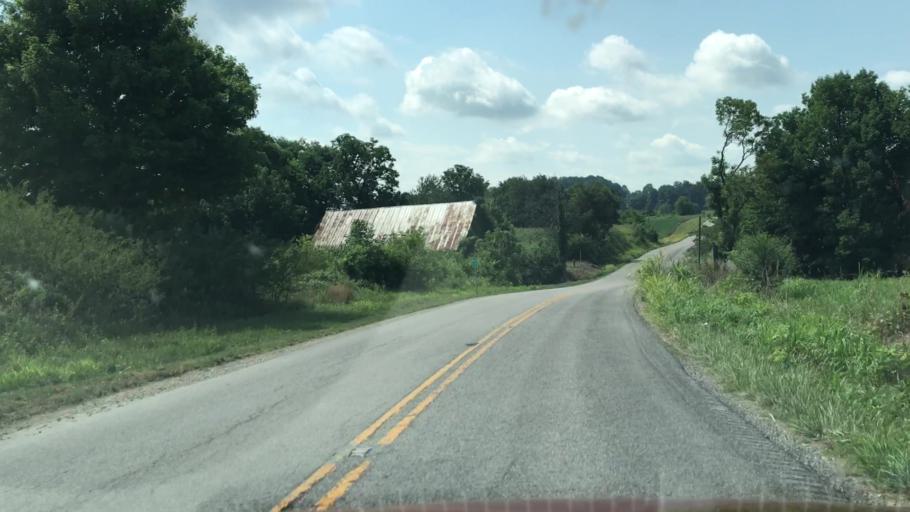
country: US
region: Kentucky
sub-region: Barren County
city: Glasgow
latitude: 36.8488
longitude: -85.8375
